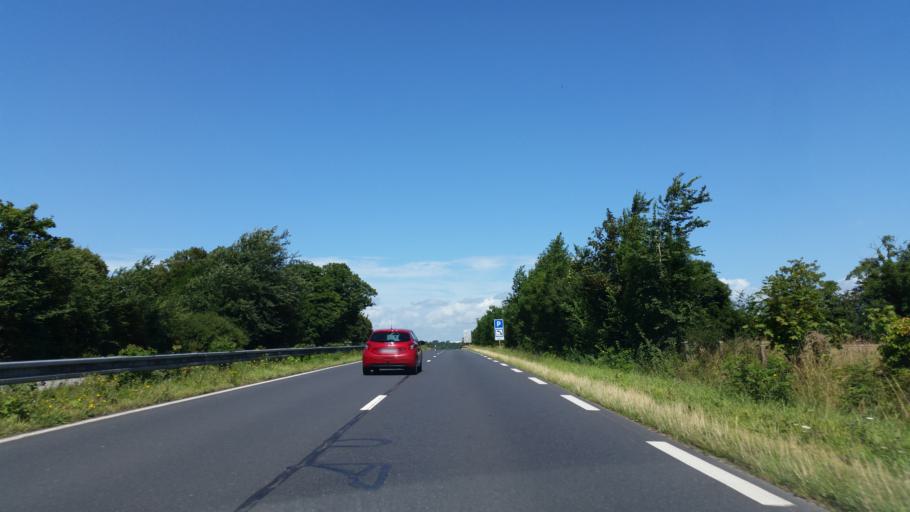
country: FR
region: Lower Normandy
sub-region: Departement de la Manche
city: Carentan
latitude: 49.3509
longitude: -1.2765
